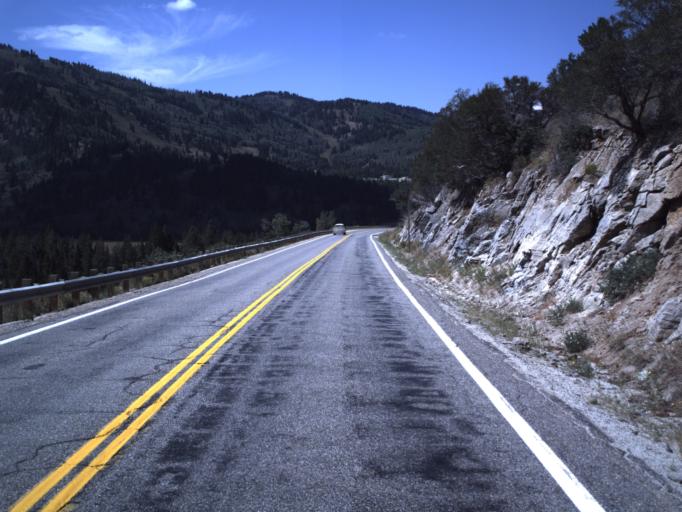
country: US
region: Idaho
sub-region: Bear Lake County
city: Paris
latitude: 41.9595
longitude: -111.5175
